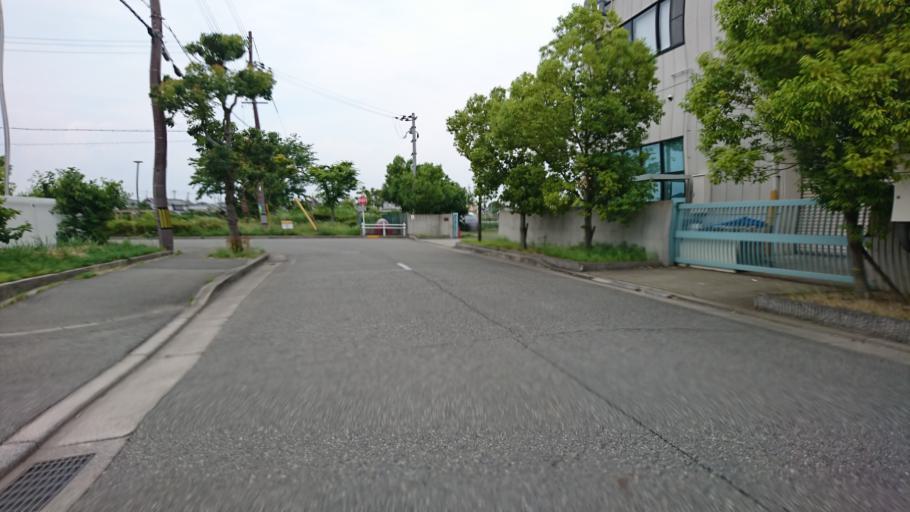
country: JP
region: Hyogo
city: Kakogawacho-honmachi
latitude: 34.7358
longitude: 134.8869
